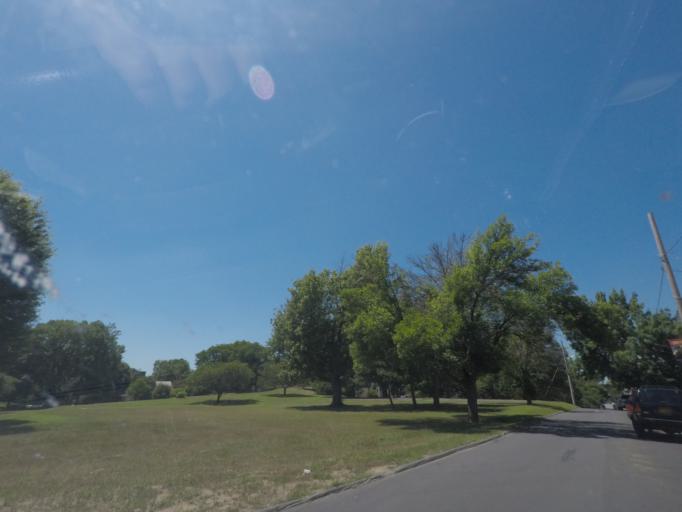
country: US
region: New York
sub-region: Rensselaer County
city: Troy
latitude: 42.7340
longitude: -73.6744
